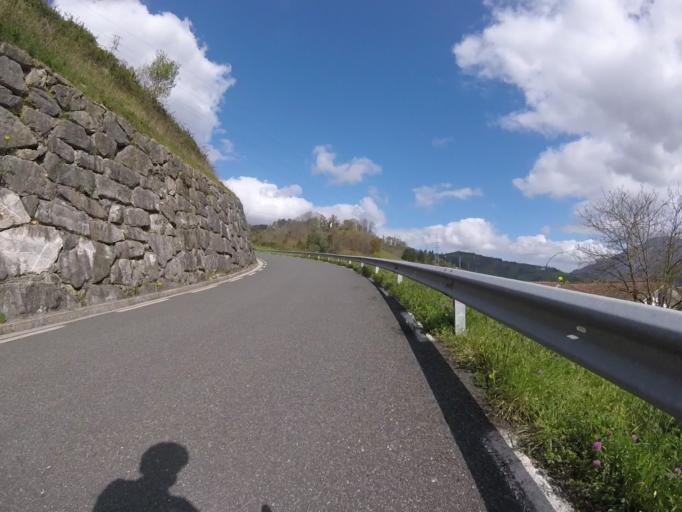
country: ES
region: Basque Country
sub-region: Provincia de Guipuzcoa
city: Tolosa
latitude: 43.1252
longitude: -2.0893
